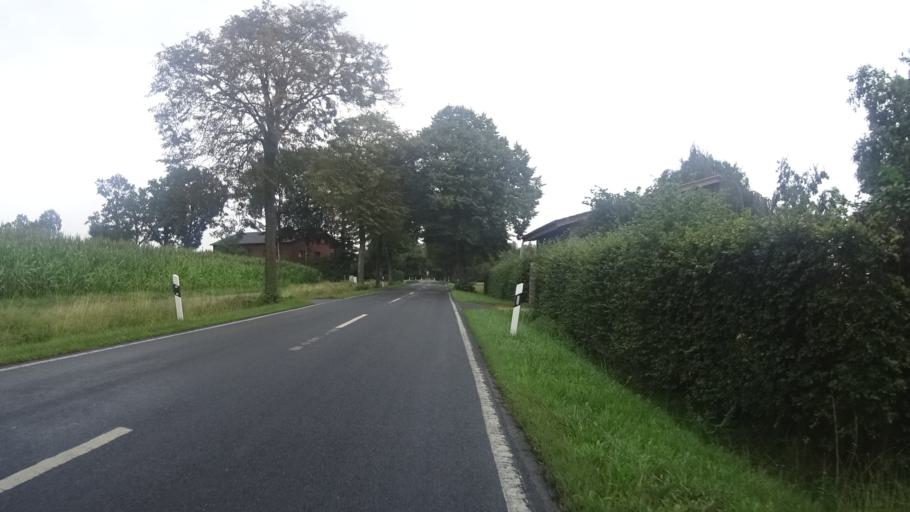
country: DE
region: Schleswig-Holstein
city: Bullenkuhlen
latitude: 53.7558
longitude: 9.7483
